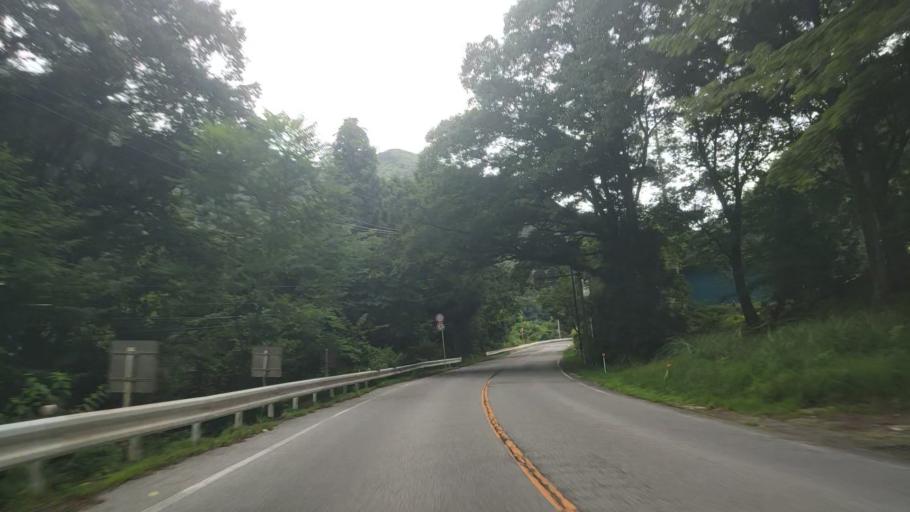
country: JP
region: Gunma
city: Omamacho-omama
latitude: 36.6068
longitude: 139.4052
